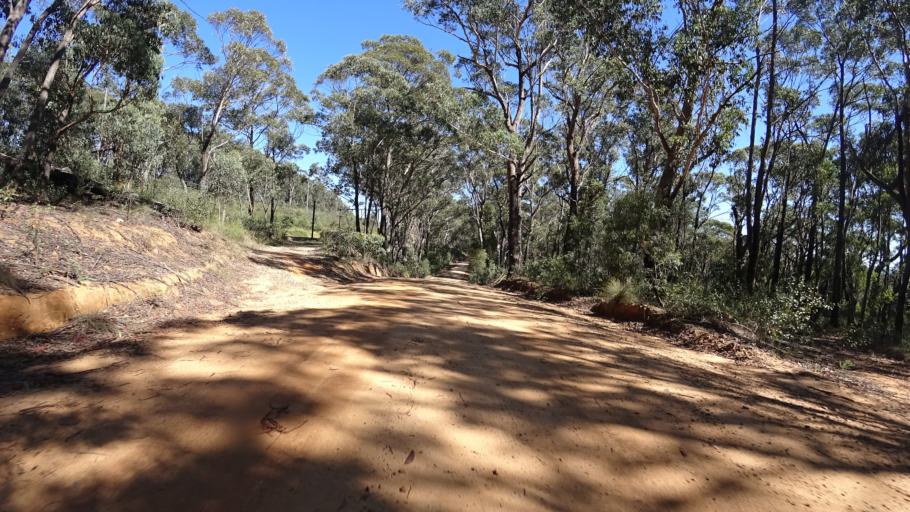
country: AU
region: New South Wales
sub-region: Lithgow
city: Lithgow
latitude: -33.4865
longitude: 150.2624
